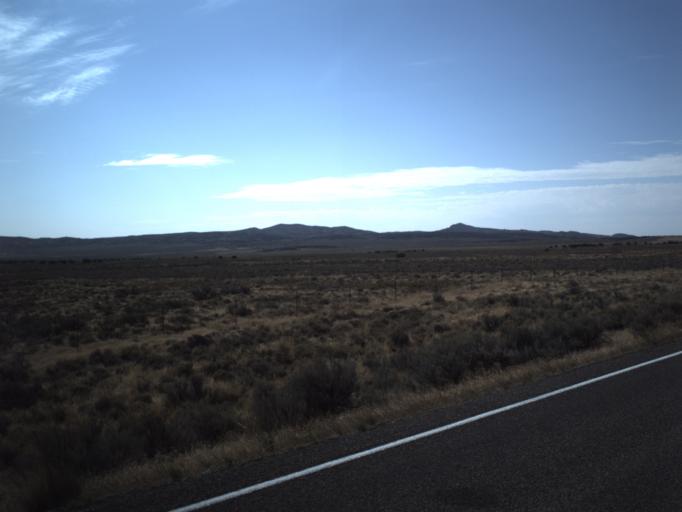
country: US
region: Idaho
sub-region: Cassia County
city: Burley
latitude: 41.7275
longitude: -113.5241
